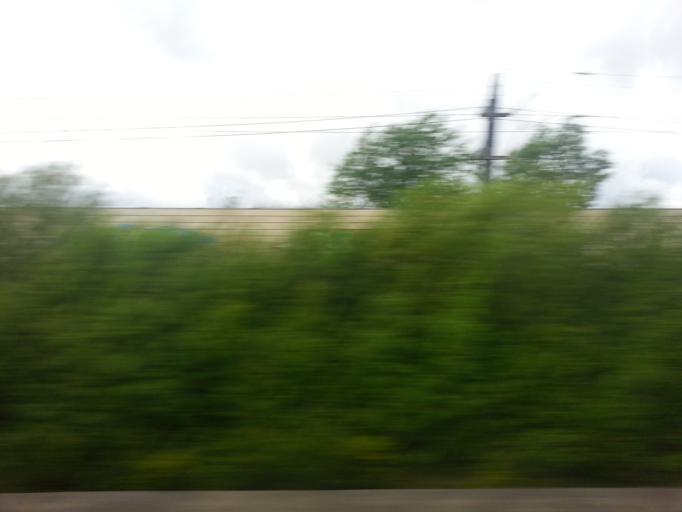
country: NO
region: Akershus
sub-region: Ullensaker
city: Klofta
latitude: 60.0654
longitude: 11.1399
